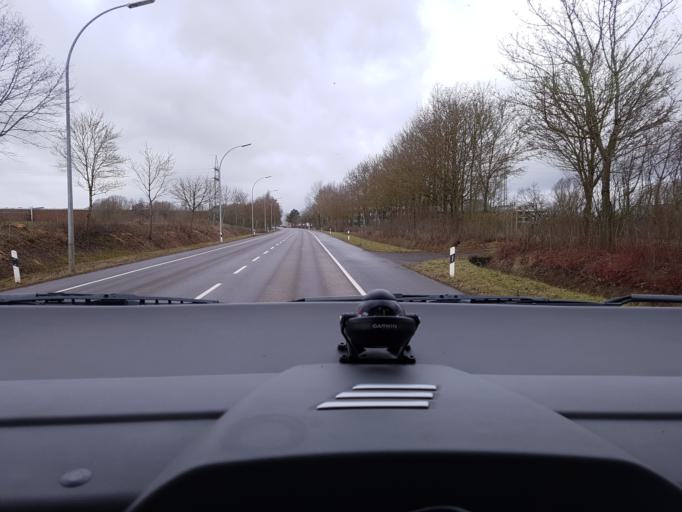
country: LU
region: Luxembourg
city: Capellen
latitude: 49.6463
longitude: 5.9690
